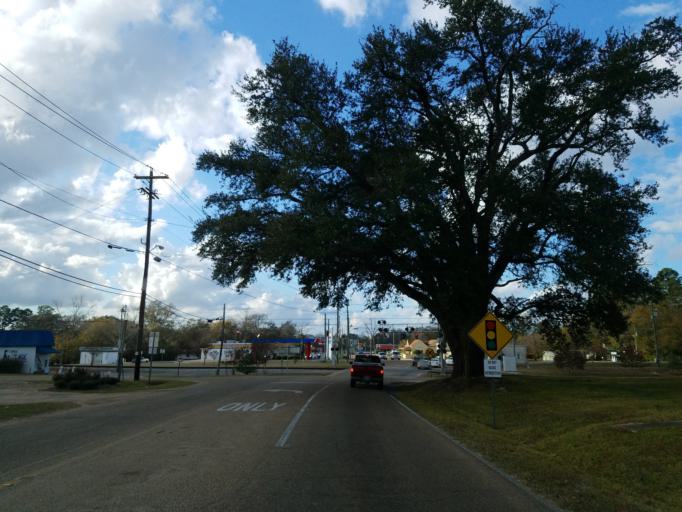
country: US
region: Mississippi
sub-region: Jones County
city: Ellisville
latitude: 31.6052
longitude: -89.1960
